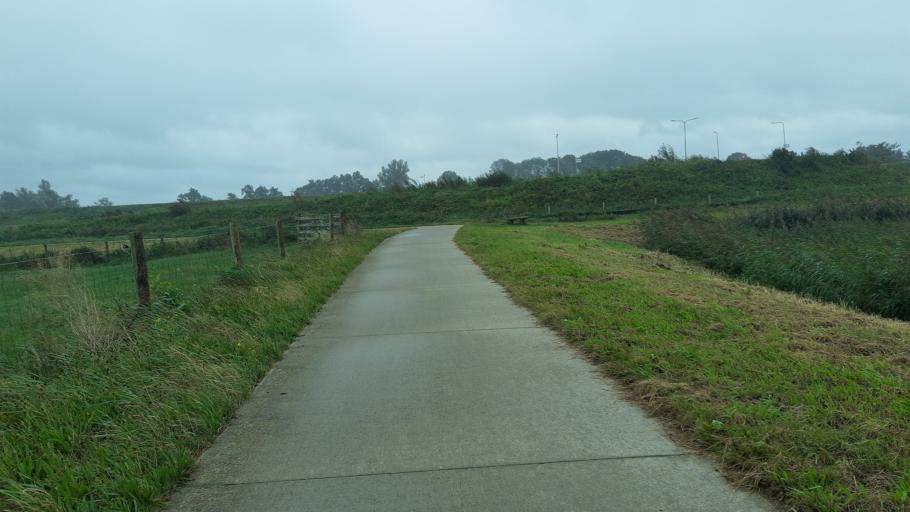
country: NL
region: Overijssel
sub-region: Gemeente Steenwijkerland
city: Blokzijl
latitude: 52.7454
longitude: 5.9935
